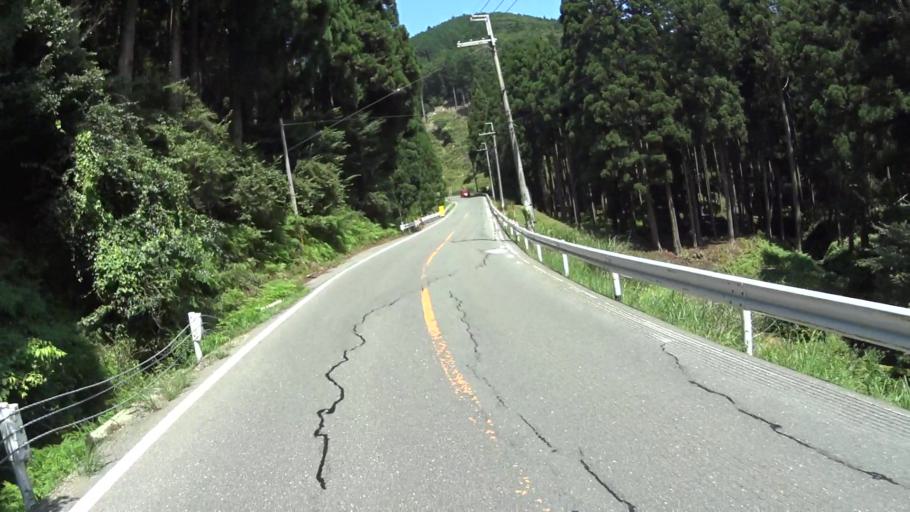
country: JP
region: Fukui
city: Obama
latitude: 35.3797
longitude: 135.9230
